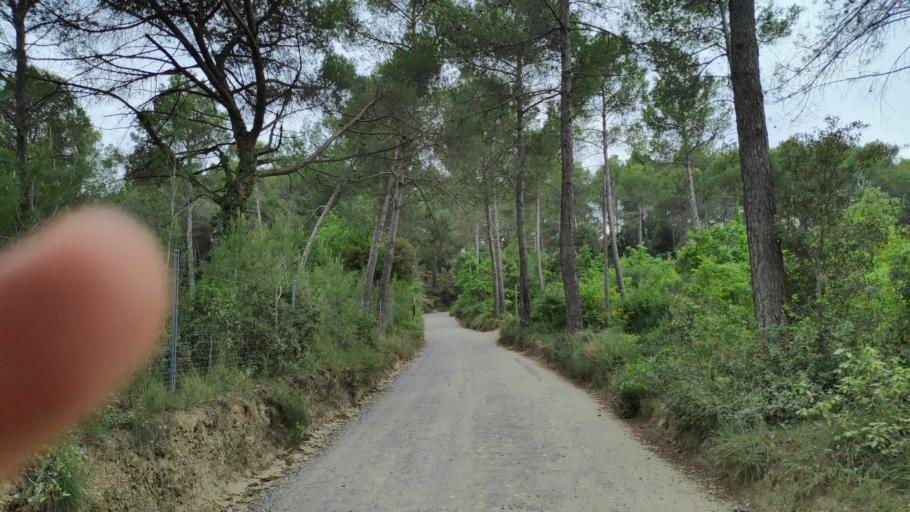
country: ES
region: Catalonia
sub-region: Provincia de Barcelona
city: Sant Quirze del Valles
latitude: 41.5105
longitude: 2.0813
